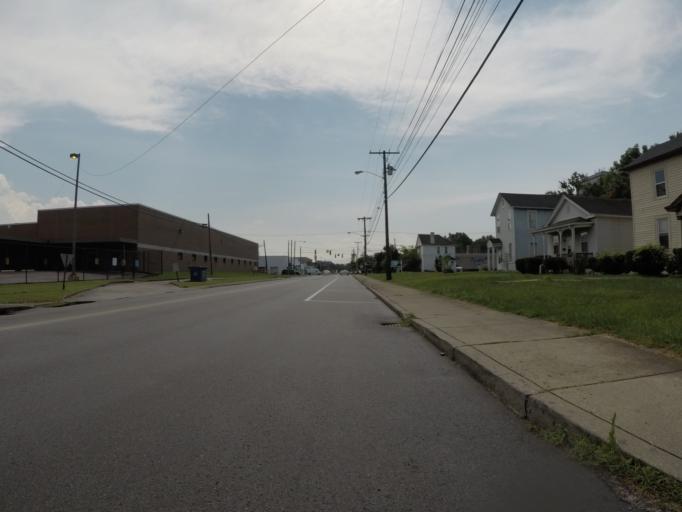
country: US
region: Kentucky
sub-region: Boyd County
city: Ashland
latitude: 38.4796
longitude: -82.6466
